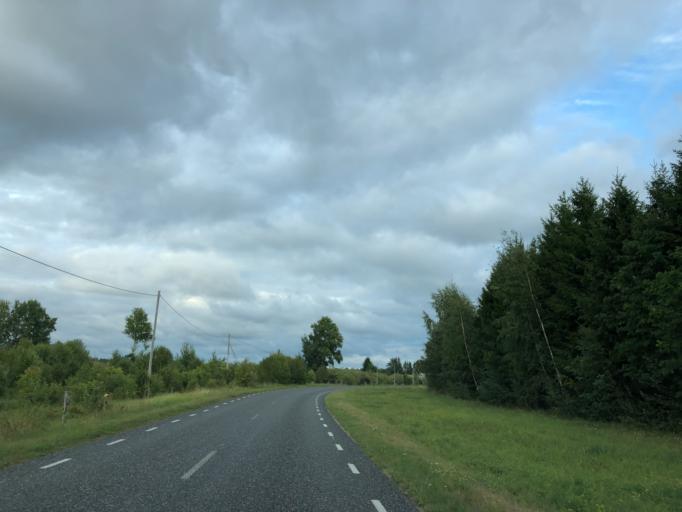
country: EE
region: Hiiumaa
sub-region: Kaerdla linn
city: Kardla
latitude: 58.7898
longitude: 22.8106
